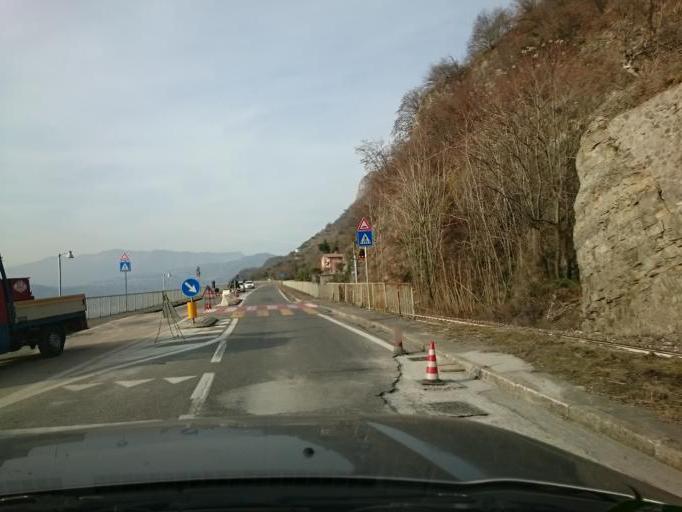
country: IT
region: Lombardy
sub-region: Provincia di Brescia
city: Marone
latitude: 45.7500
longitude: 10.0865
